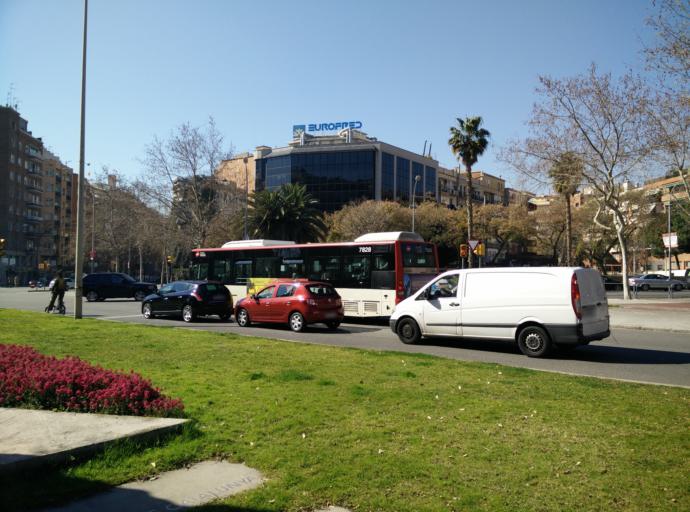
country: ES
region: Catalonia
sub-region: Provincia de Barcelona
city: les Corts
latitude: 41.3861
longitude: 2.1427
